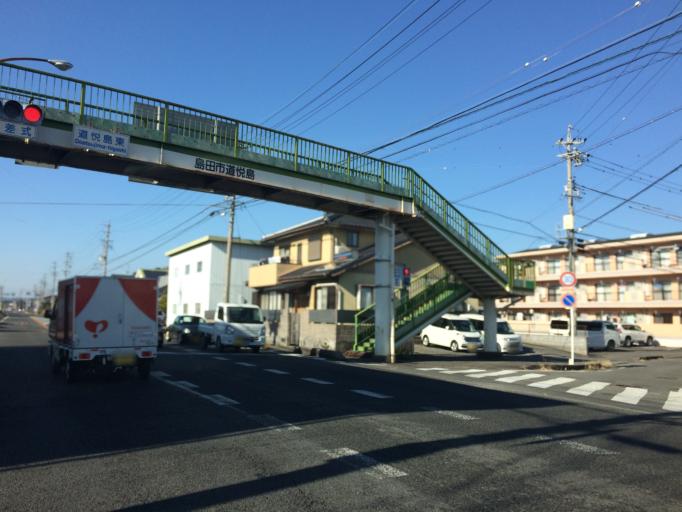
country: JP
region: Shizuoka
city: Shimada
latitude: 34.8386
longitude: 138.2092
